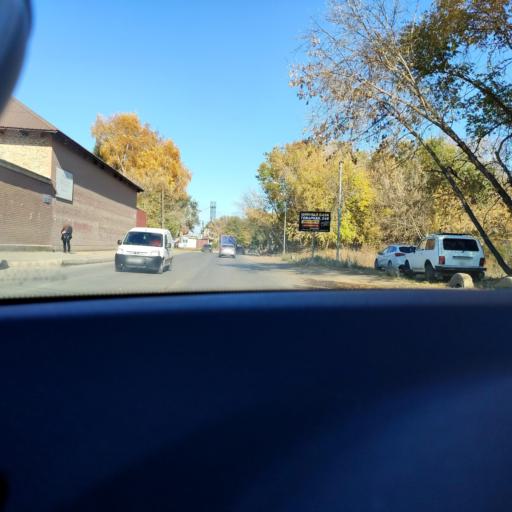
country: RU
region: Samara
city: Petra-Dubrava
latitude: 53.2355
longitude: 50.2941
